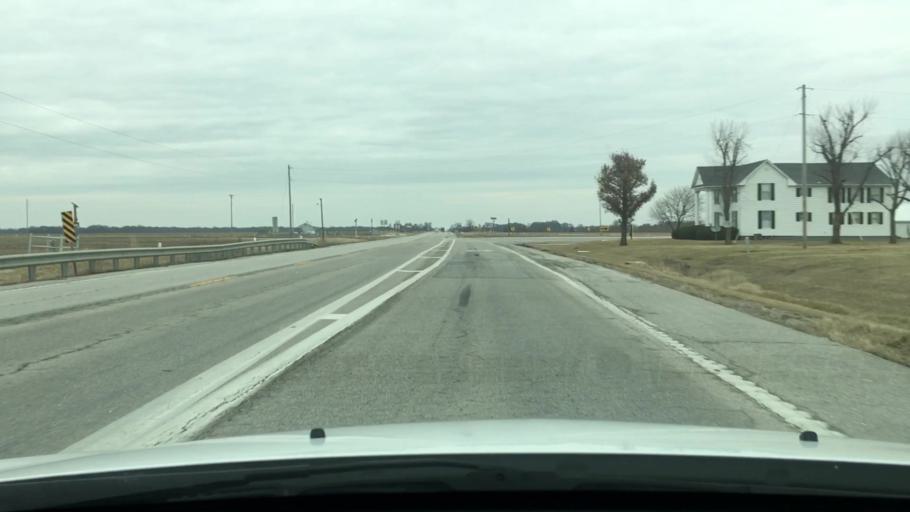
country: US
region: Missouri
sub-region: Audrain County
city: Vandalia
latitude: 39.2791
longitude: -91.6442
